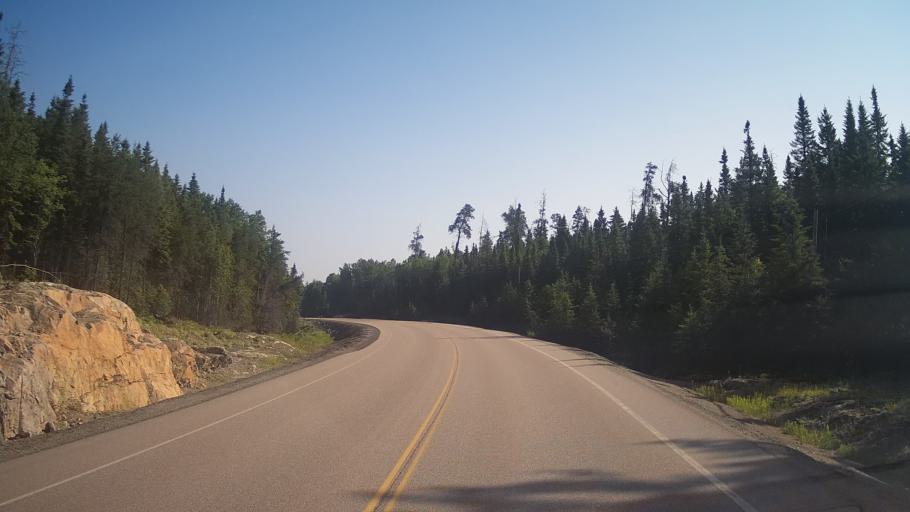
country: CA
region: Ontario
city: Rayside-Balfour
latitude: 47.0271
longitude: -81.6376
